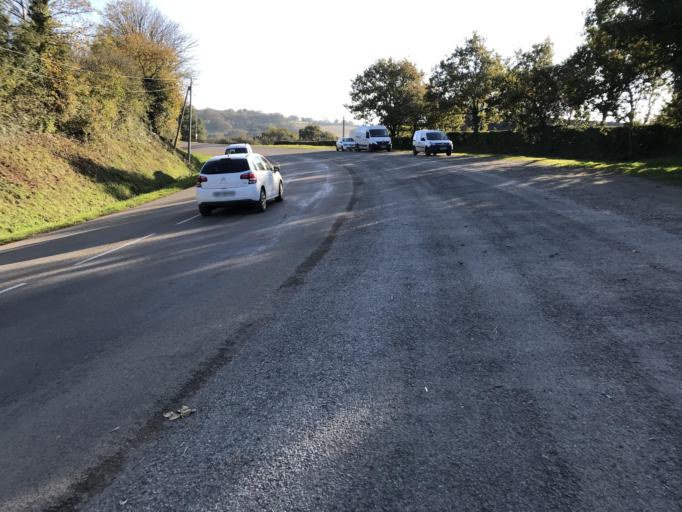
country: FR
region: Brittany
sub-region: Departement du Finistere
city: Hopital-Camfrout
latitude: 48.3160
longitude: -4.2289
